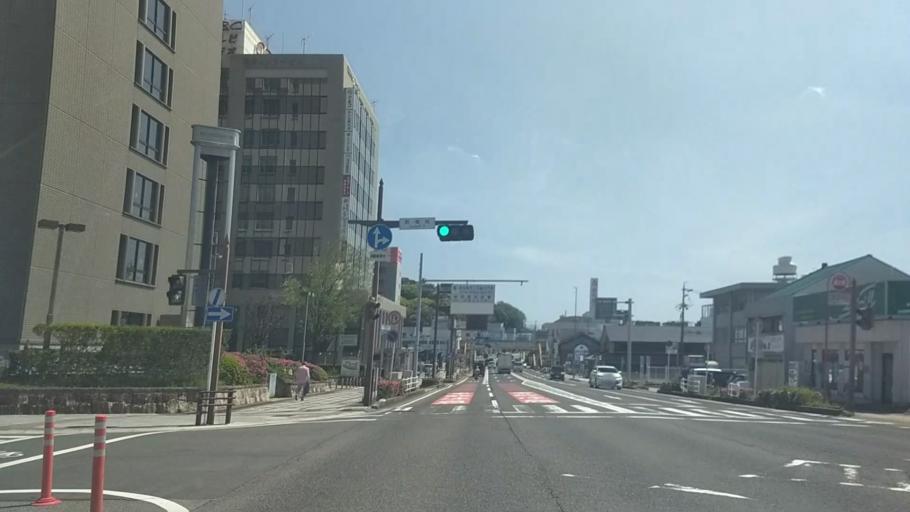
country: JP
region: Aichi
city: Okazaki
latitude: 34.9549
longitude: 137.1641
